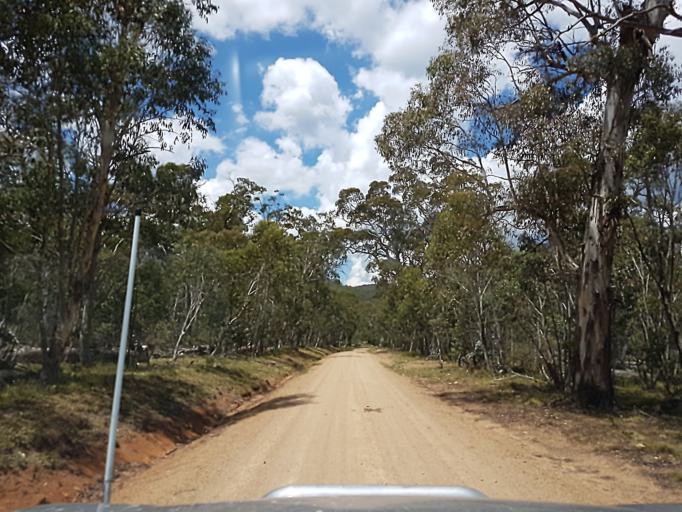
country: AU
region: New South Wales
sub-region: Snowy River
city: Jindabyne
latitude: -36.8922
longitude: 148.0868
